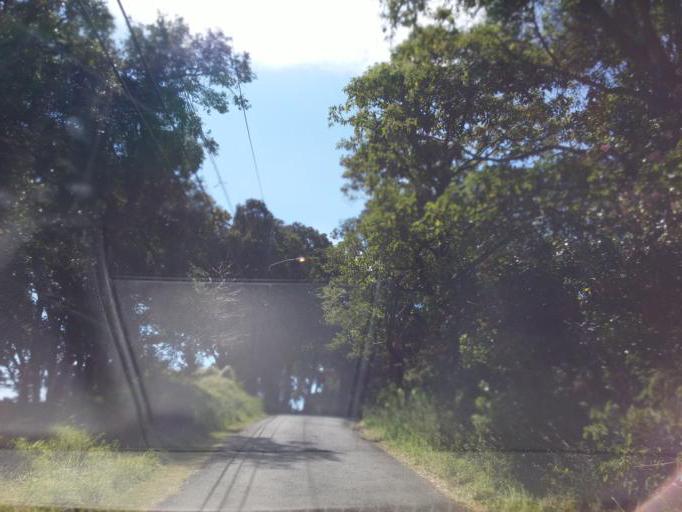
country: CR
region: Heredia
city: Santo Domingo
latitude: 10.1013
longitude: -84.1186
